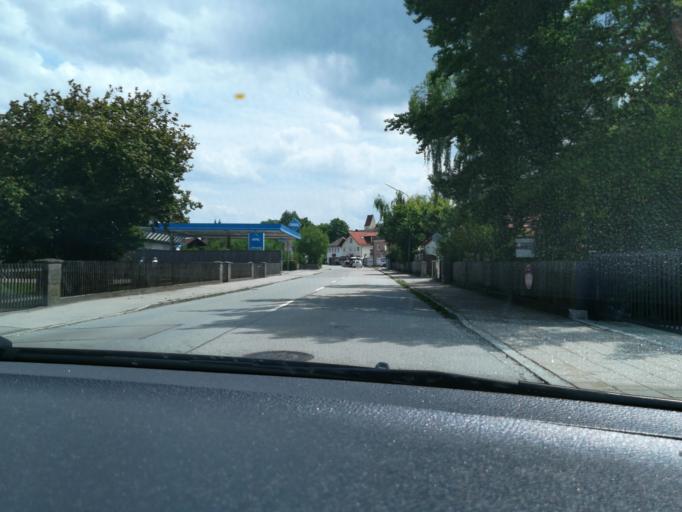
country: DE
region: Bavaria
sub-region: Upper Bavaria
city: Hohenkirchen-Siegertsbrunn
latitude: 48.0200
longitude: 11.7090
